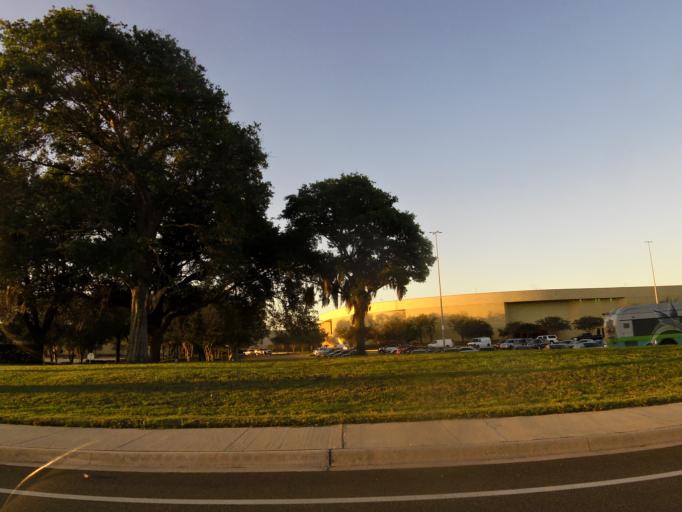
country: NO
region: Oppland
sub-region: Nord-Fron
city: Vinstra
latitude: 61.6115
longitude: 9.6398
